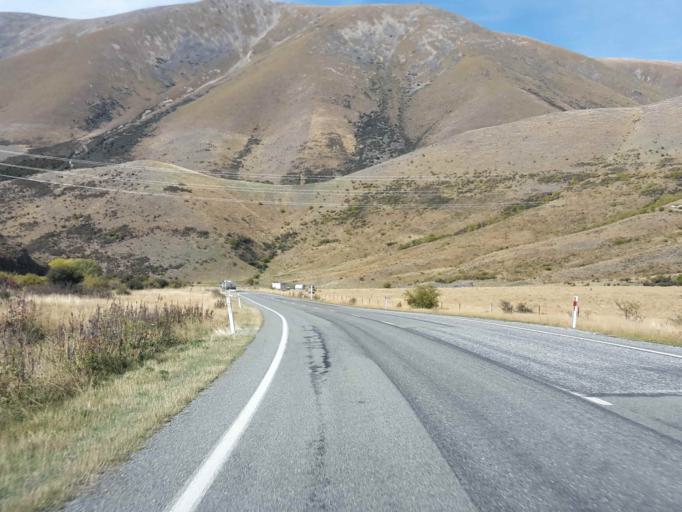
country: NZ
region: Otago
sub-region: Queenstown-Lakes District
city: Wanaka
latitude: -44.5610
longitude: 169.6815
